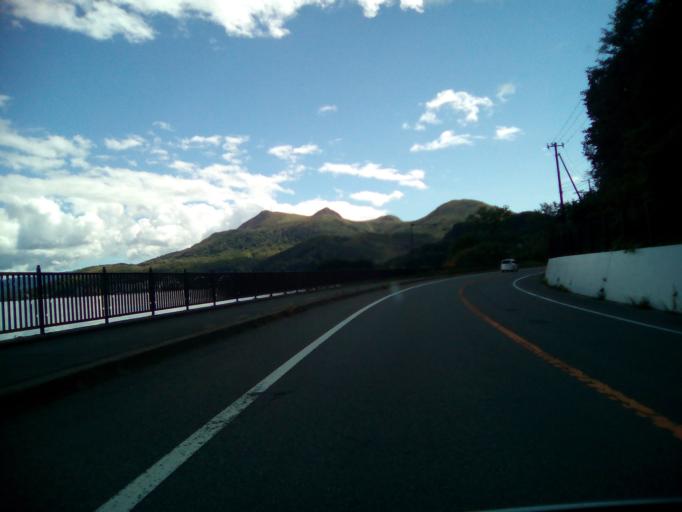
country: JP
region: Hokkaido
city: Date
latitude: 42.5778
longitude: 140.7979
